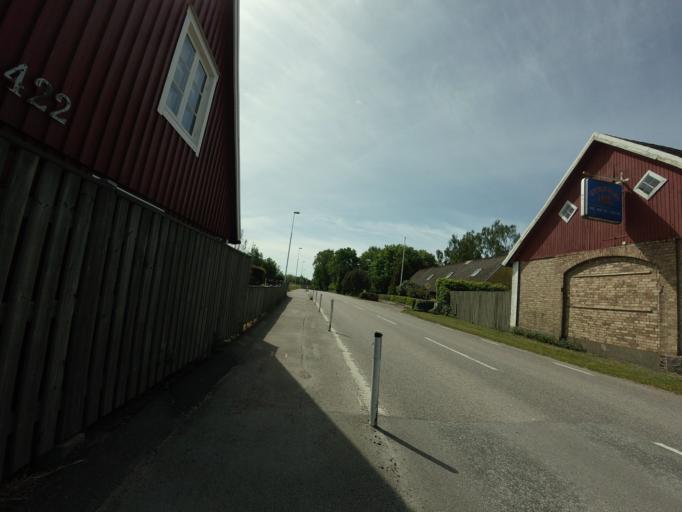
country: SE
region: Skane
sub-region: Helsingborg
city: Odakra
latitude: 56.1290
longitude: 12.6936
